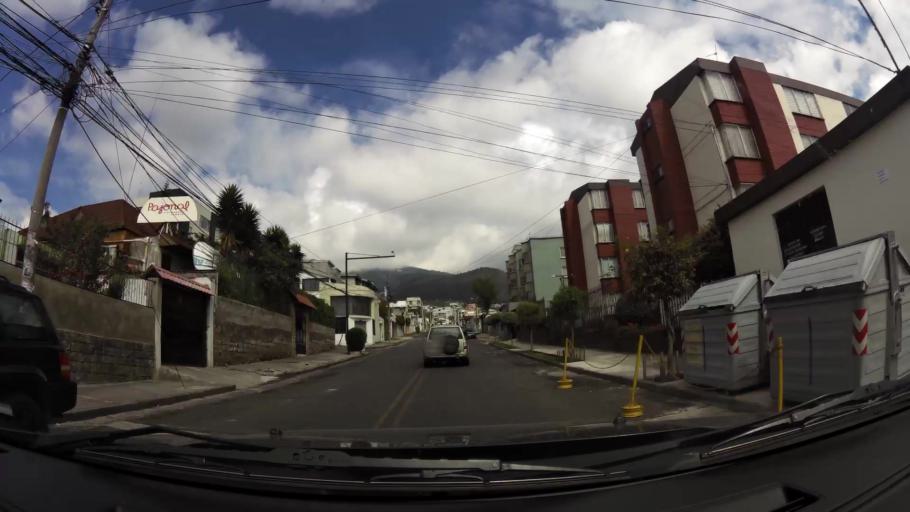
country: EC
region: Pichincha
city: Quito
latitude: -0.1462
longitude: -78.4945
